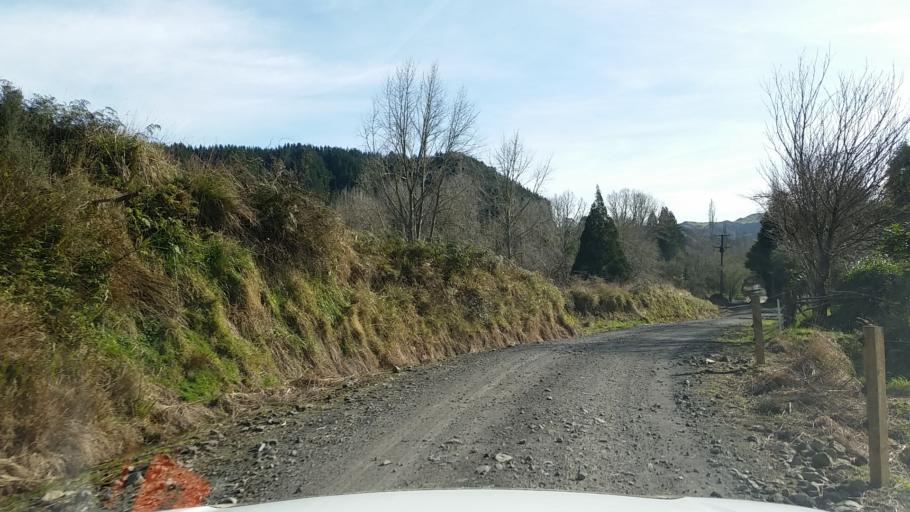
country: NZ
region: Taranaki
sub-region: South Taranaki District
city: Eltham
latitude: -39.3608
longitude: 174.5134
